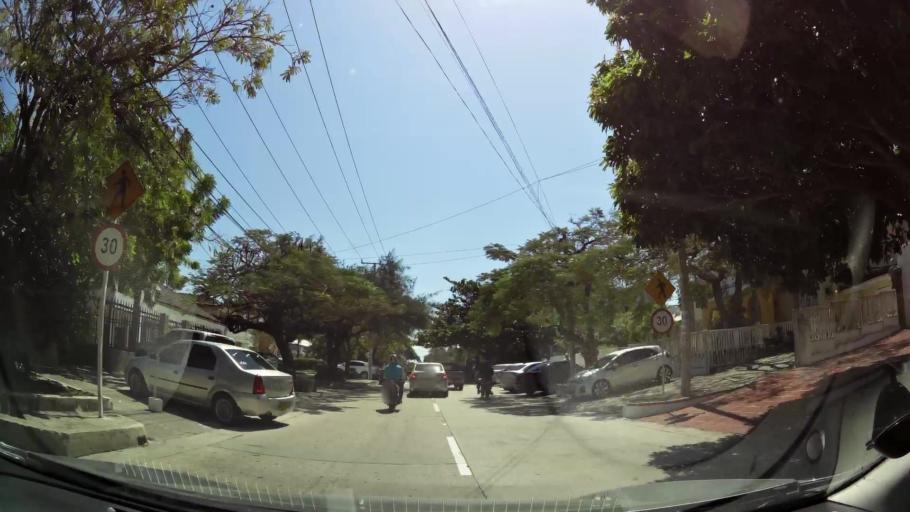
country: CO
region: Atlantico
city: Barranquilla
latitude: 11.0016
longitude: -74.7974
